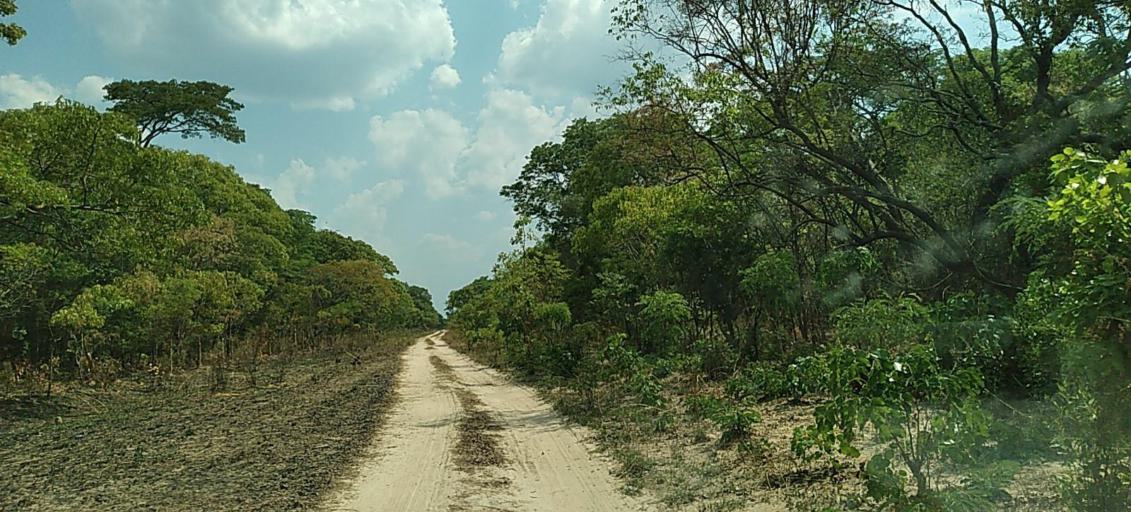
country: ZM
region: Copperbelt
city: Mpongwe
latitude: -13.8404
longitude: 27.9358
